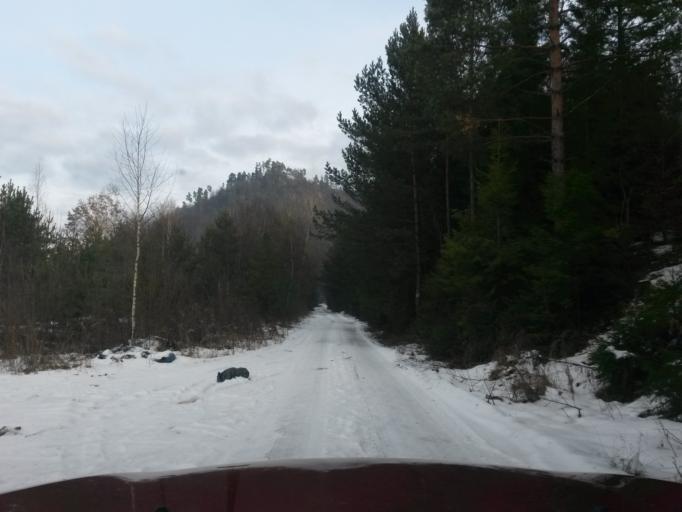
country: SK
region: Kosicky
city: Spisska Nova Ves
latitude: 48.8949
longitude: 20.6359
